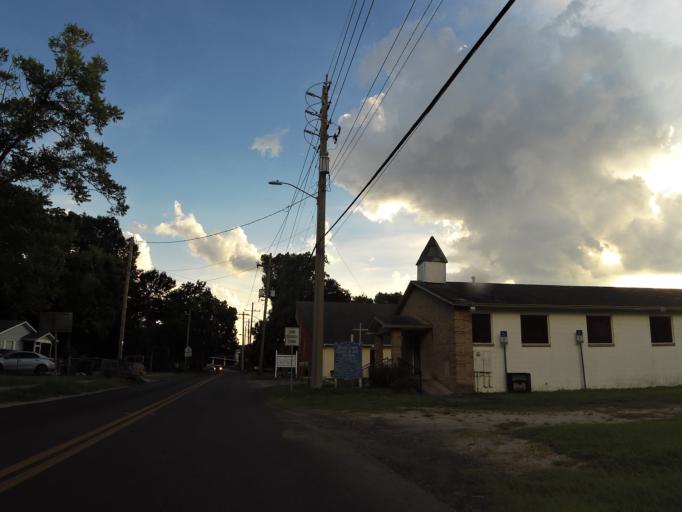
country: US
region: Florida
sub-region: Duval County
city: Jacksonville
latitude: 30.3385
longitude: -81.6879
